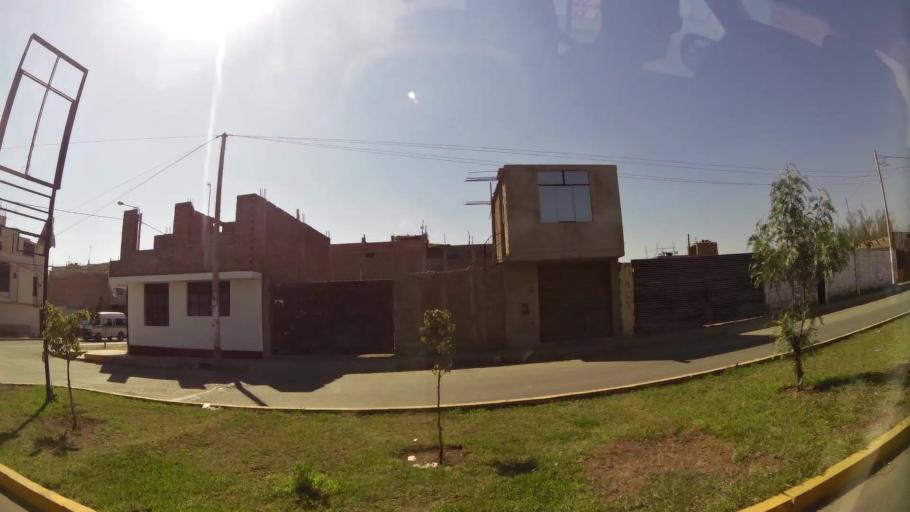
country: PE
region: Ica
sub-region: Provincia de Ica
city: La Tinguina
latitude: -14.0346
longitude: -75.7028
